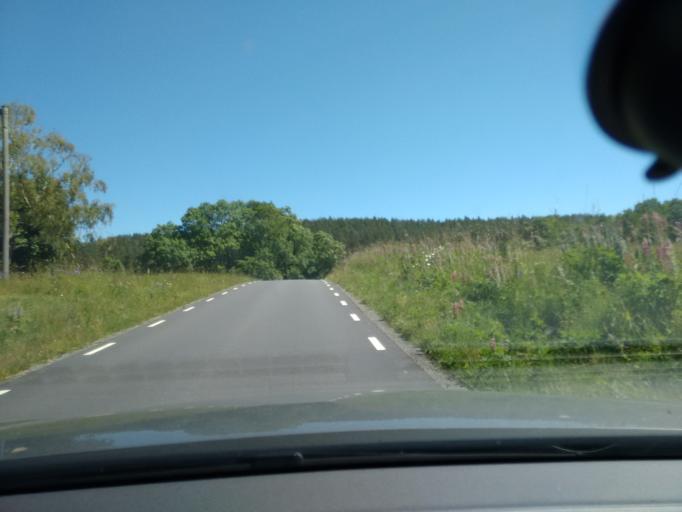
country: SE
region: Skane
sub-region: Kristianstads Kommun
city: Degeberga
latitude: 55.7758
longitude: 14.1206
